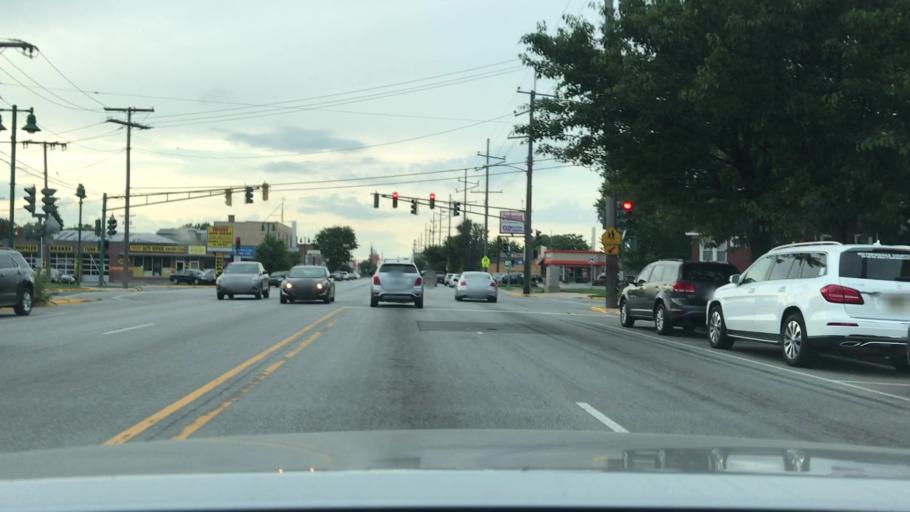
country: US
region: Indiana
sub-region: Lake County
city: Whiting
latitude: 41.6843
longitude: -87.5045
